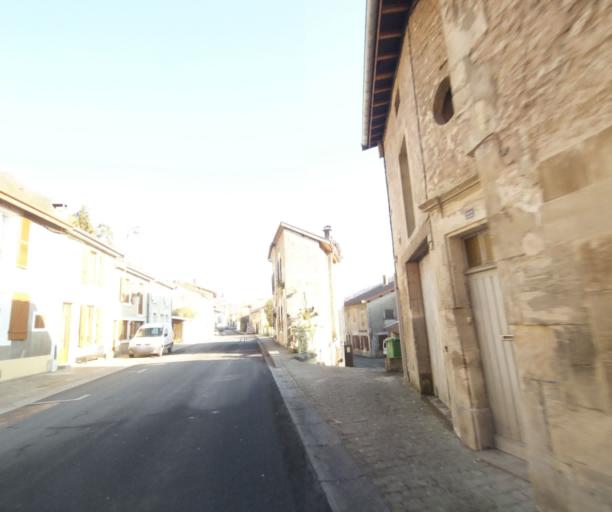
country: FR
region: Champagne-Ardenne
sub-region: Departement de la Haute-Marne
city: Chevillon
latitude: 48.5289
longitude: 5.1285
